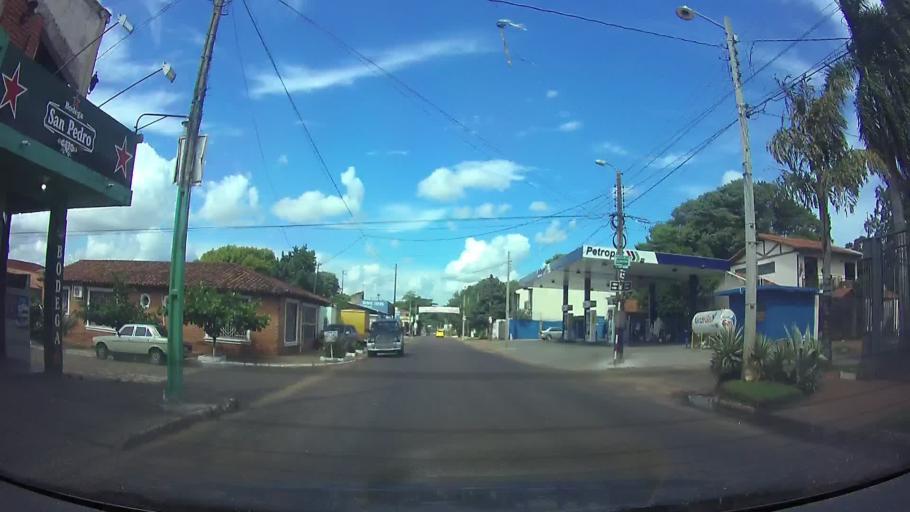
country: PY
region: Central
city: Villa Elisa
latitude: -25.3431
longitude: -57.5770
